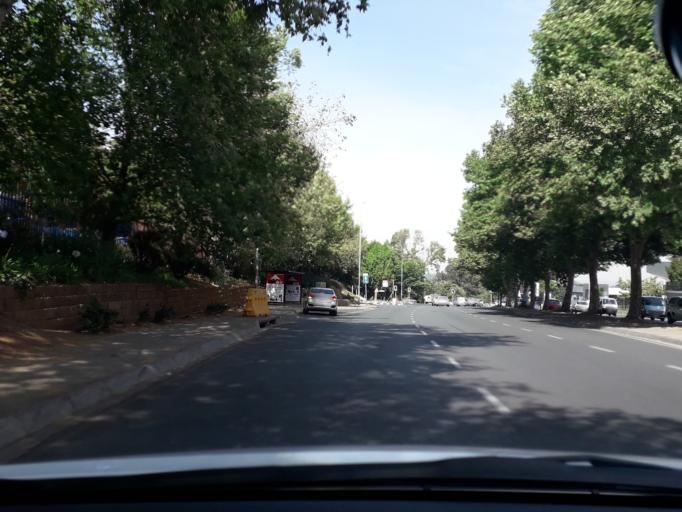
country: ZA
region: Gauteng
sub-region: City of Johannesburg Metropolitan Municipality
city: Johannesburg
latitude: -26.1003
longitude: 28.0520
